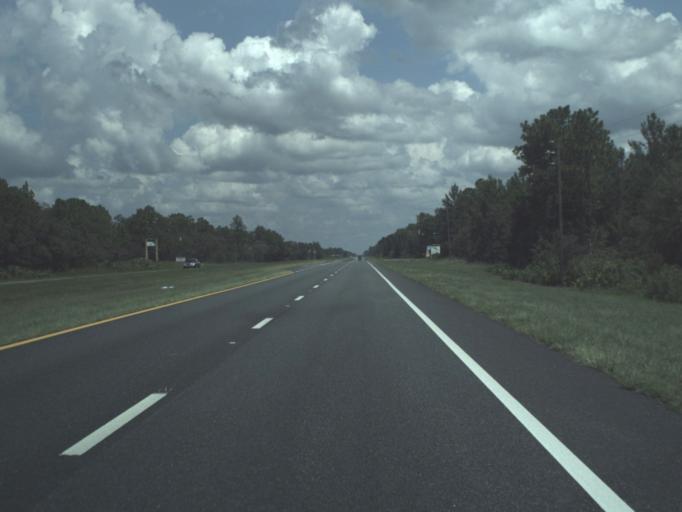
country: US
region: Florida
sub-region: Citrus County
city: Sugarmill Woods
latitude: 28.6804
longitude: -82.5522
